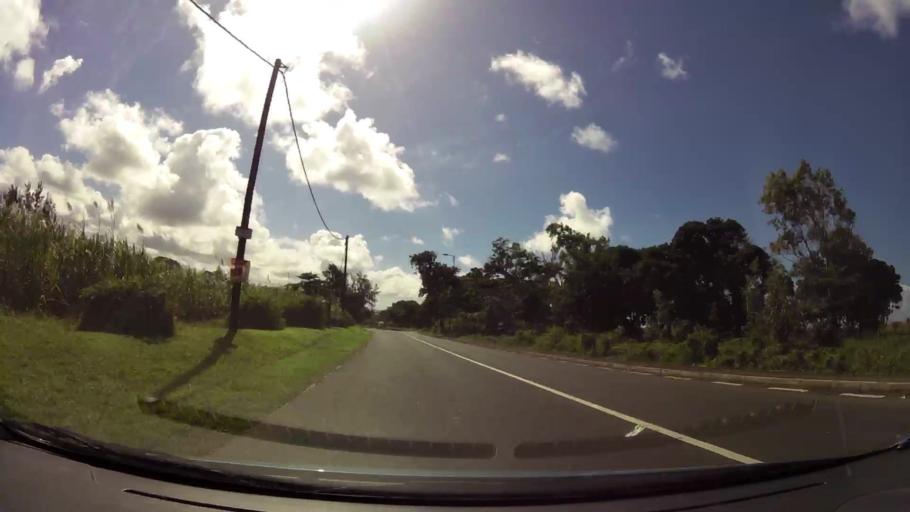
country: MU
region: Grand Port
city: Beau Vallon
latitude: -20.4234
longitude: 57.7012
